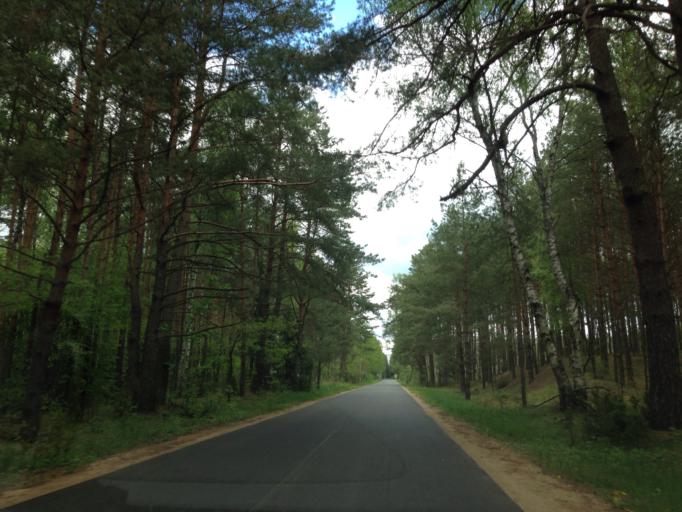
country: PL
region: Podlasie
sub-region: Powiat grajewski
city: Radzilow
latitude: 53.3487
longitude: 22.5974
